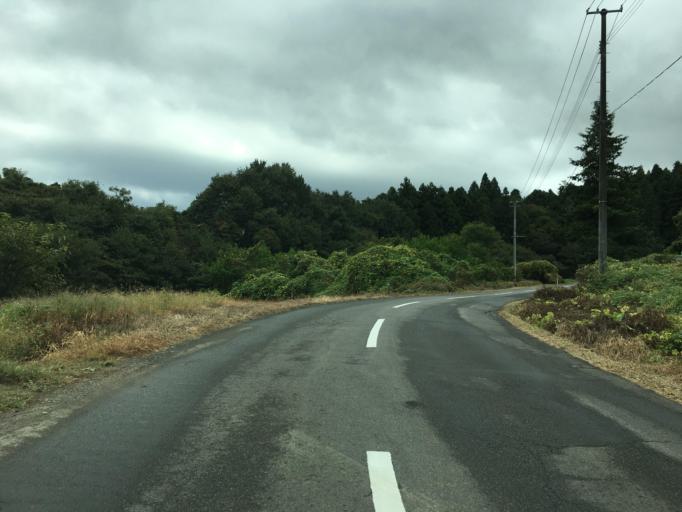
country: JP
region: Fukushima
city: Nihommatsu
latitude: 37.6313
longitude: 140.4375
